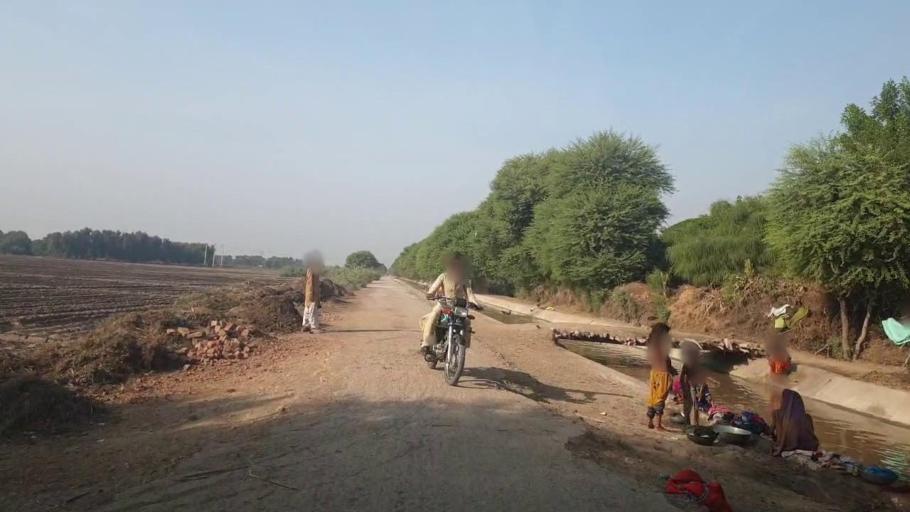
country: PK
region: Sindh
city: Tando Jam
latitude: 25.4212
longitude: 68.4624
